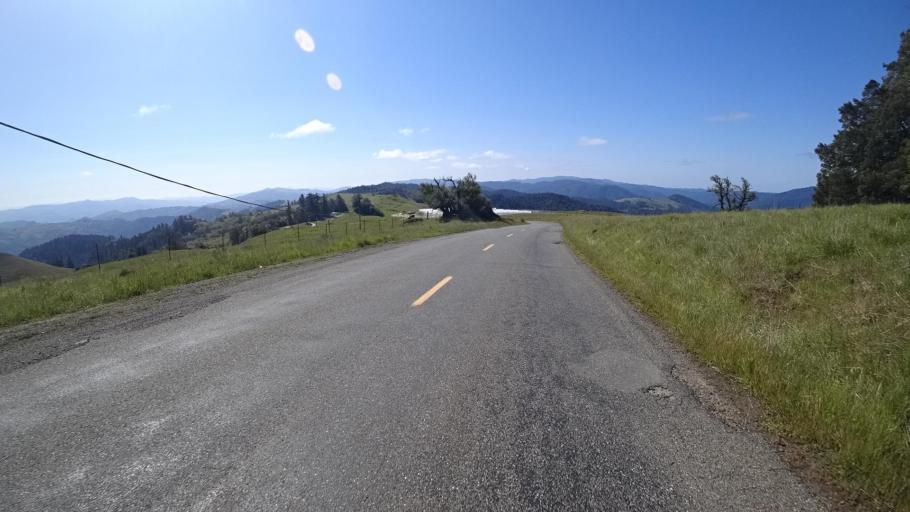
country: US
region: California
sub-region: Humboldt County
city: Redway
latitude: 40.0905
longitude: -123.6774
